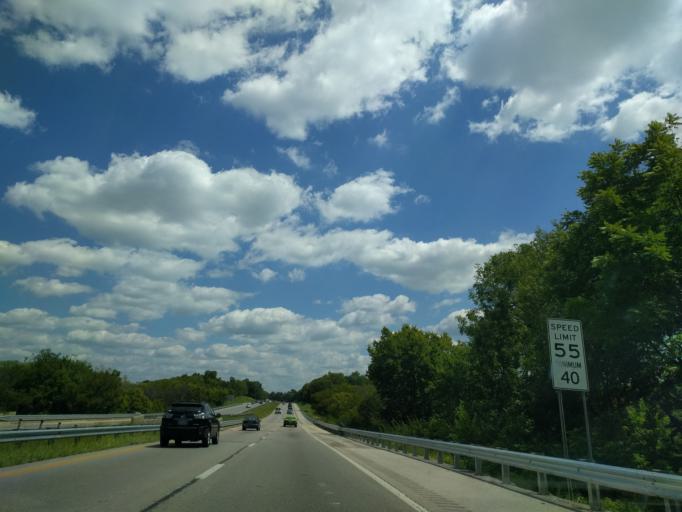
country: US
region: Kentucky
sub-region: Fayette County
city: Lexington
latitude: 37.9918
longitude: -84.4829
